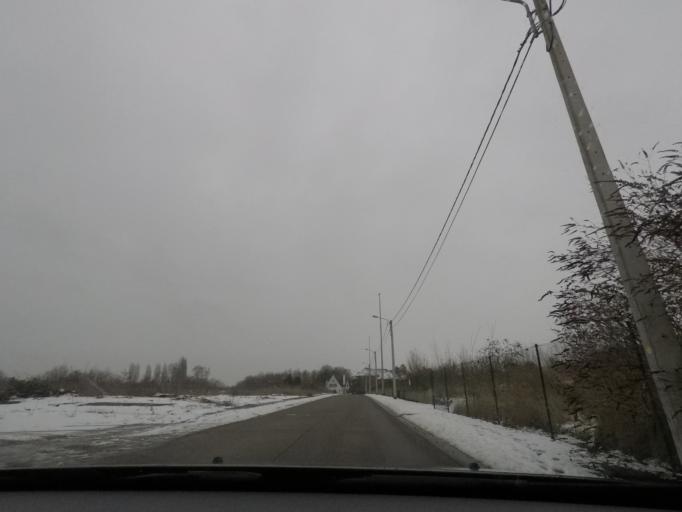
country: BE
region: Wallonia
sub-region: Province du Hainaut
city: Brugelette
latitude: 50.5940
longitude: 3.8567
